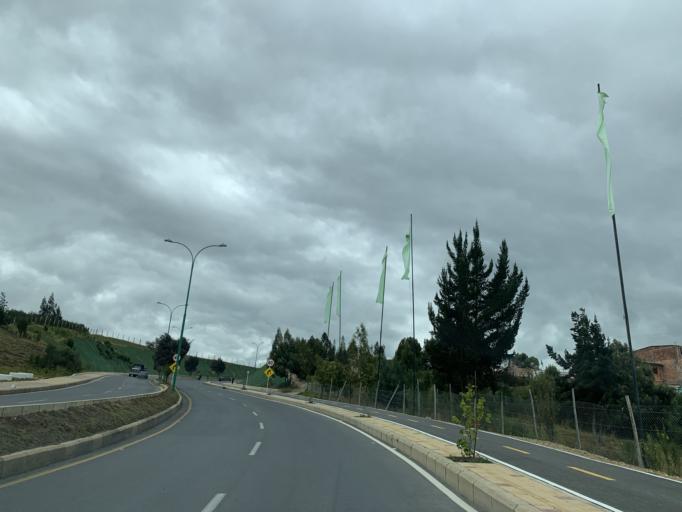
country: CO
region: Boyaca
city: Tunja
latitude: 5.5371
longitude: -73.3470
